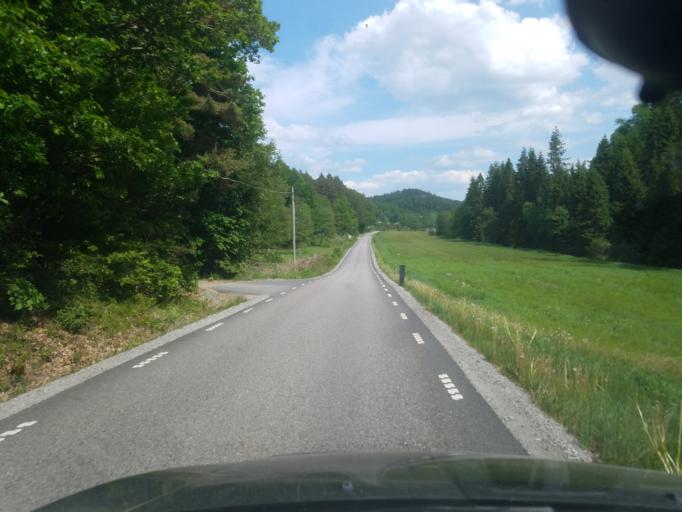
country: SE
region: Vaestra Goetaland
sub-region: Stenungsunds Kommun
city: Stora Hoga
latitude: 58.0165
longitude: 11.9137
